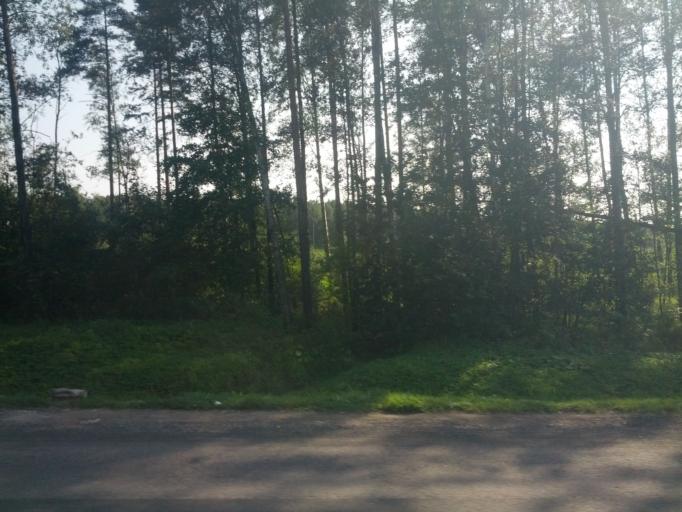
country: RU
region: Leningrad
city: Rybatskoye
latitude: 59.8925
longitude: 30.5422
